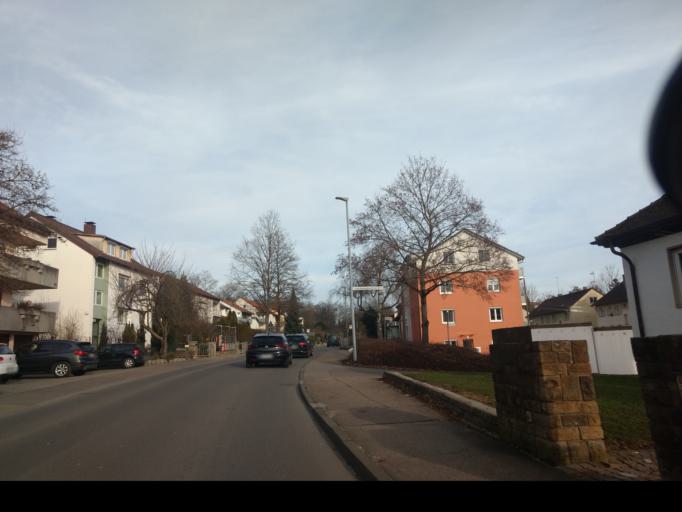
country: DE
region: Baden-Wuerttemberg
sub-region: Regierungsbezirk Stuttgart
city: Wangen
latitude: 48.7157
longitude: 9.6247
